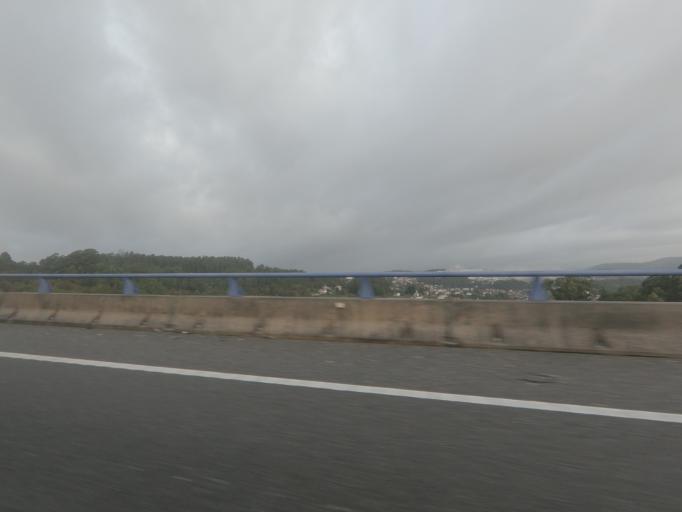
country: ES
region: Galicia
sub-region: Provincia de Pontevedra
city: Porrino
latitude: 42.1892
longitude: -8.6564
